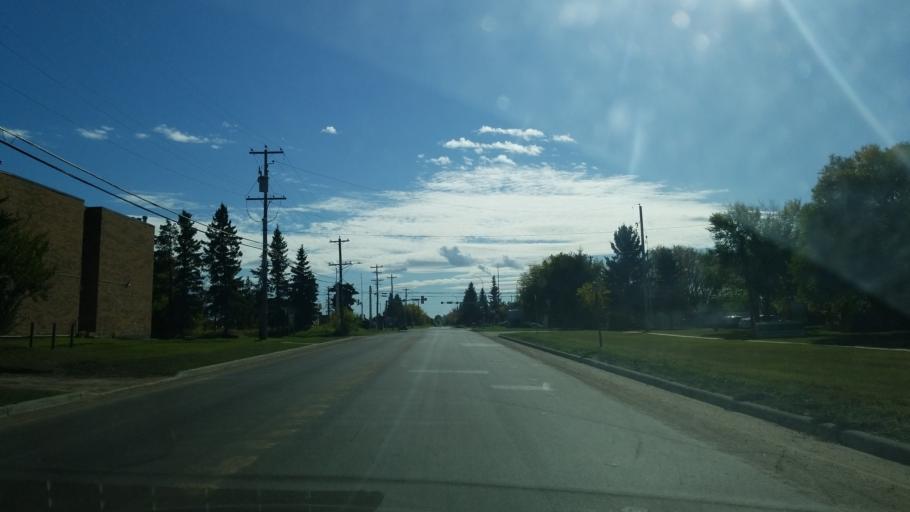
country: CA
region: Saskatchewan
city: Lloydminster
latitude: 53.2795
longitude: -109.9914
